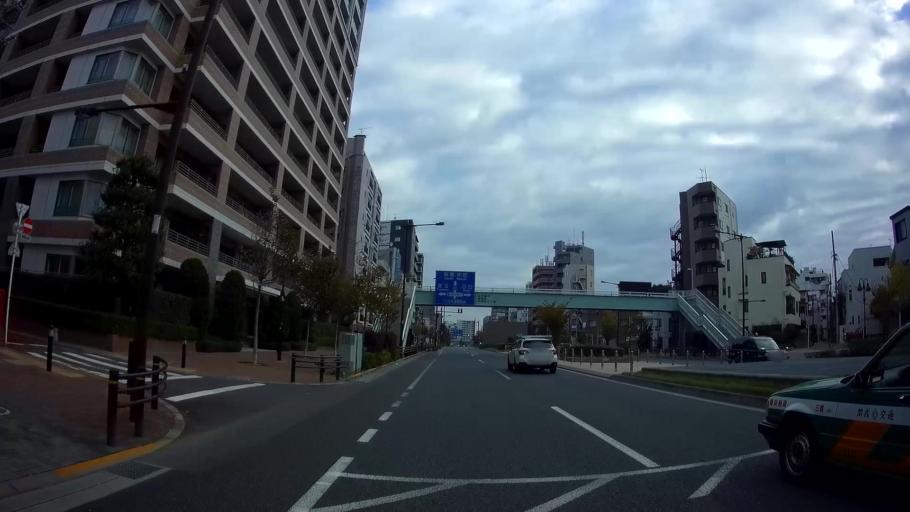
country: JP
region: Tokyo
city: Tokyo
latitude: 35.7202
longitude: 139.6901
